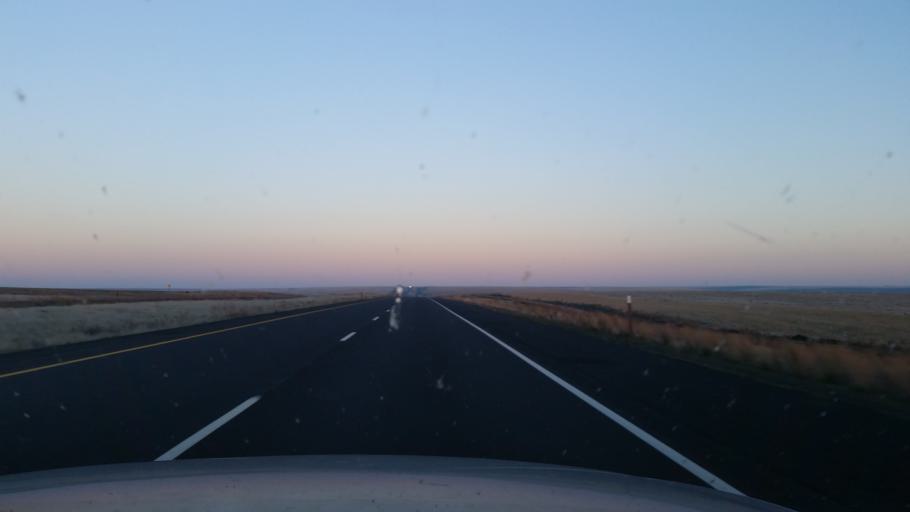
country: US
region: Washington
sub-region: Grant County
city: Warden
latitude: 47.0860
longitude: -118.7765
